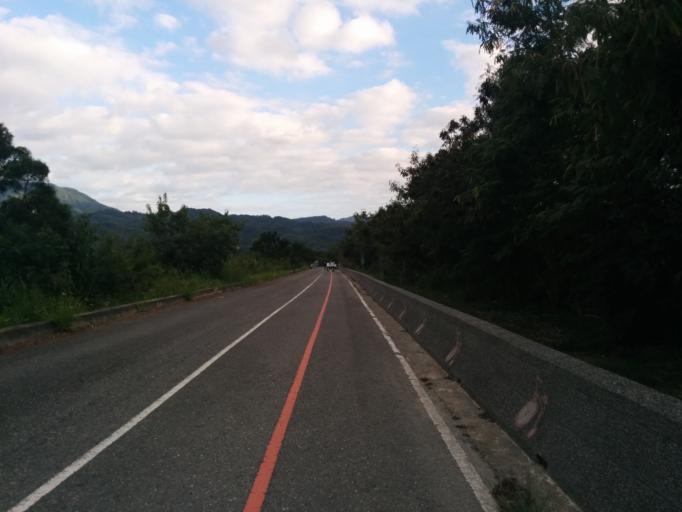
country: TW
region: Taiwan
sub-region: Taitung
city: Taitung
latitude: 23.0263
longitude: 121.1597
